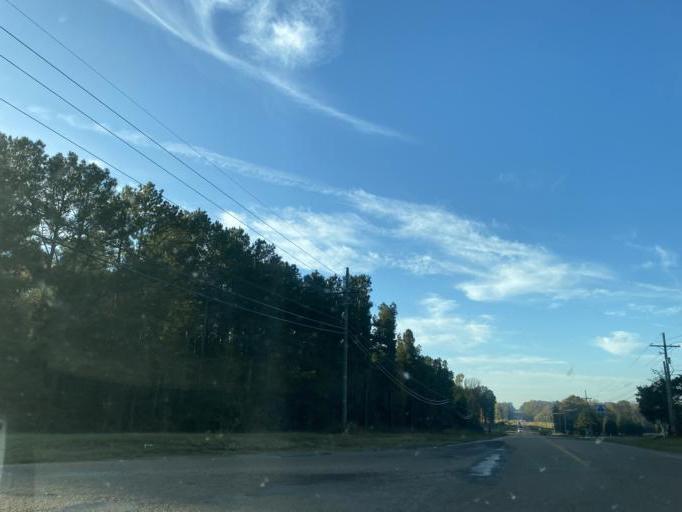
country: US
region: Mississippi
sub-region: Madison County
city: Madison
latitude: 32.4925
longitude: -90.0955
